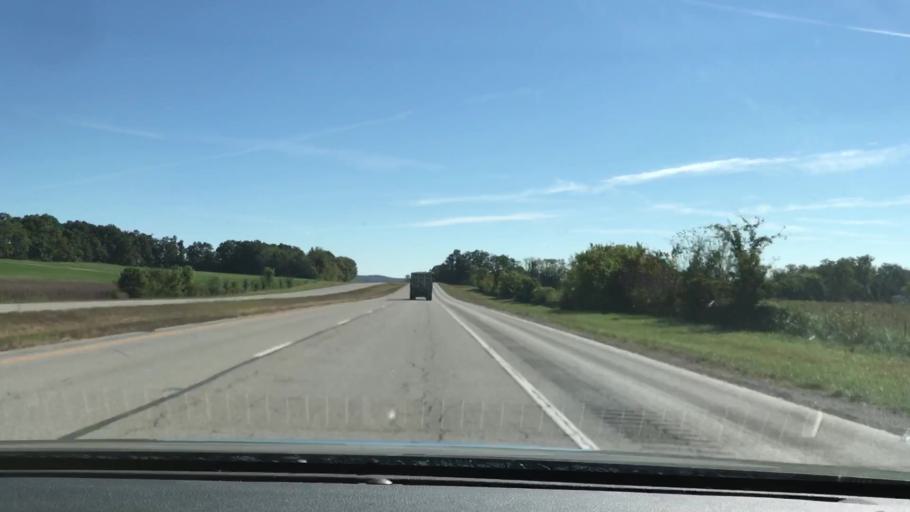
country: US
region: Kentucky
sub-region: Todd County
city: Elkton
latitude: 36.8465
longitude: -87.2969
